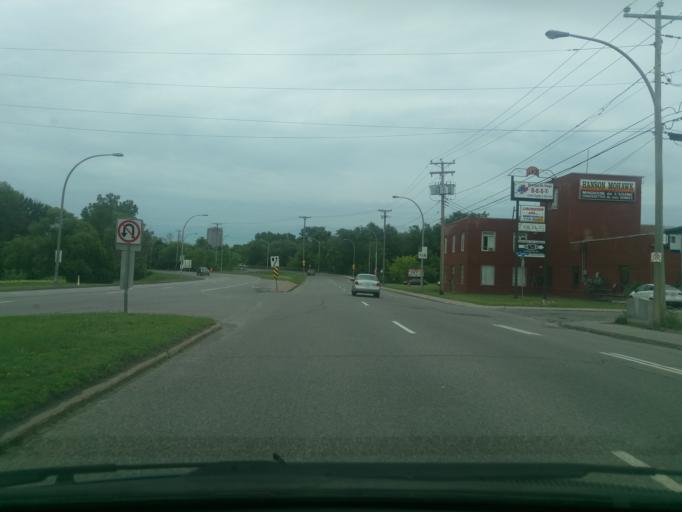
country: CA
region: Quebec
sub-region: Outaouais
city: Gatineau
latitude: 45.4442
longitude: -75.7133
